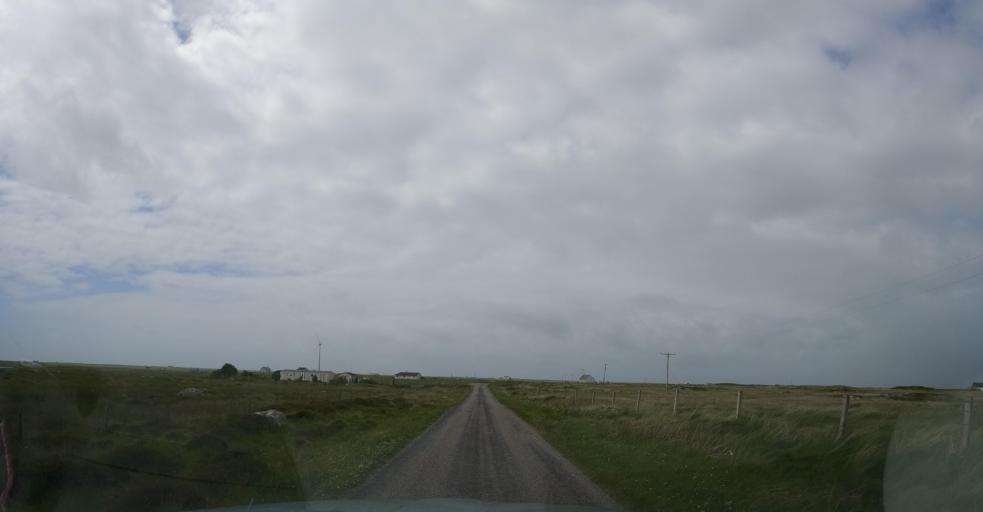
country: GB
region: Scotland
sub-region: Eilean Siar
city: Isle of South Uist
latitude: 57.2409
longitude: -7.3942
